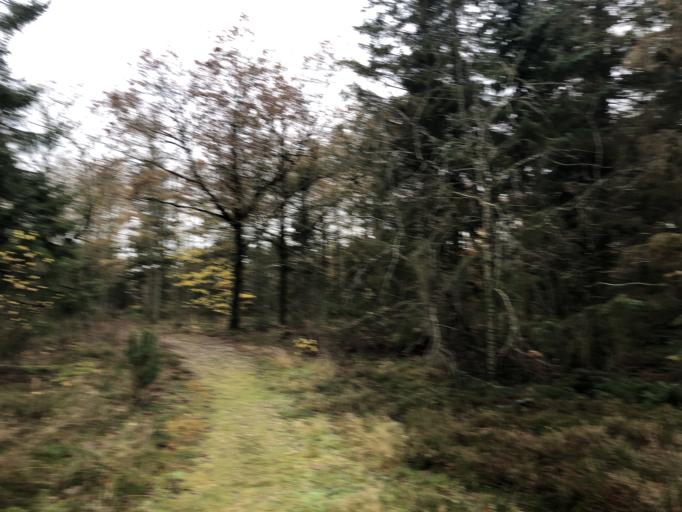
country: DK
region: Central Jutland
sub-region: Holstebro Kommune
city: Ulfborg
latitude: 56.3143
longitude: 8.2036
